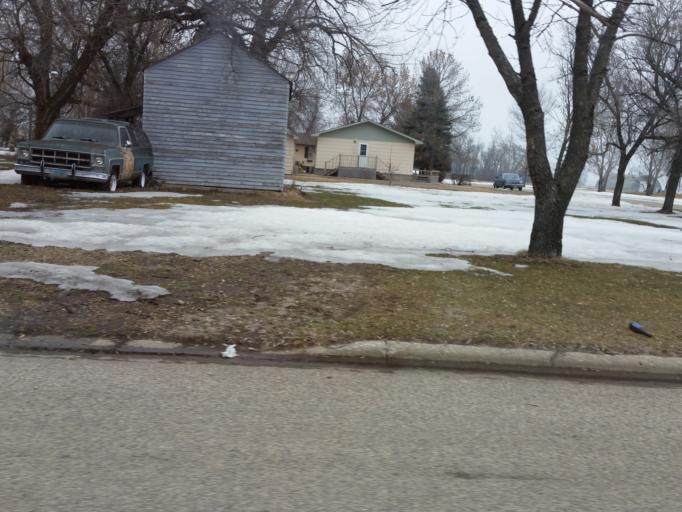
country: US
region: North Dakota
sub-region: Walsh County
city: Grafton
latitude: 48.6213
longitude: -97.4455
